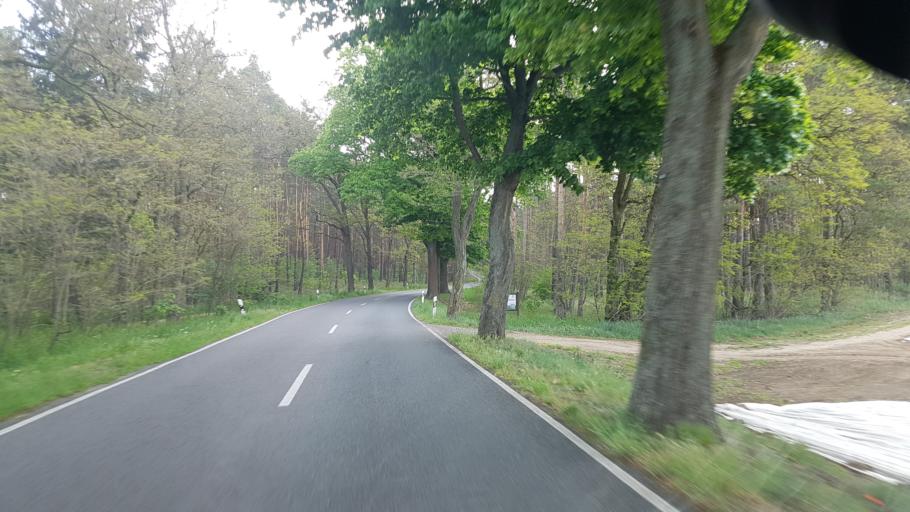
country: DE
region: Brandenburg
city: Baruth
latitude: 51.9710
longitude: 13.4462
